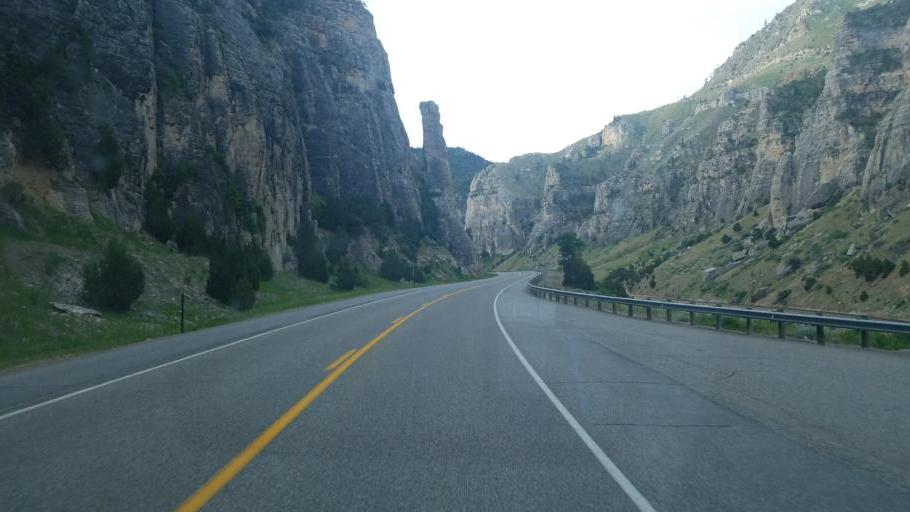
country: US
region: Wyoming
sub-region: Hot Springs County
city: Thermopolis
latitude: 43.5363
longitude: -108.1794
